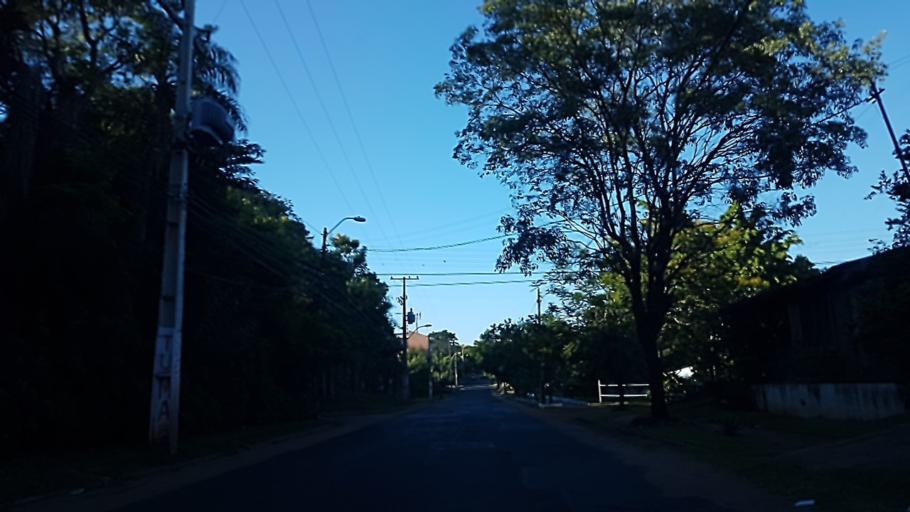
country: PY
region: Central
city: Fernando de la Mora
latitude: -25.2645
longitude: -57.5599
